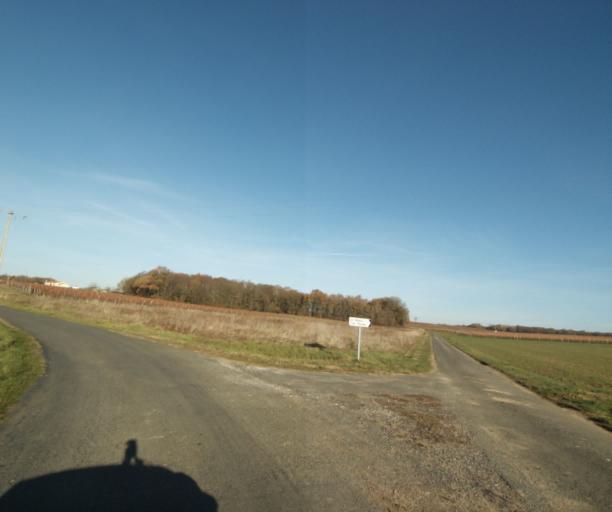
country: FR
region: Poitou-Charentes
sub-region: Departement de la Charente-Maritime
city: Cherac
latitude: 45.7263
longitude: -0.4447
